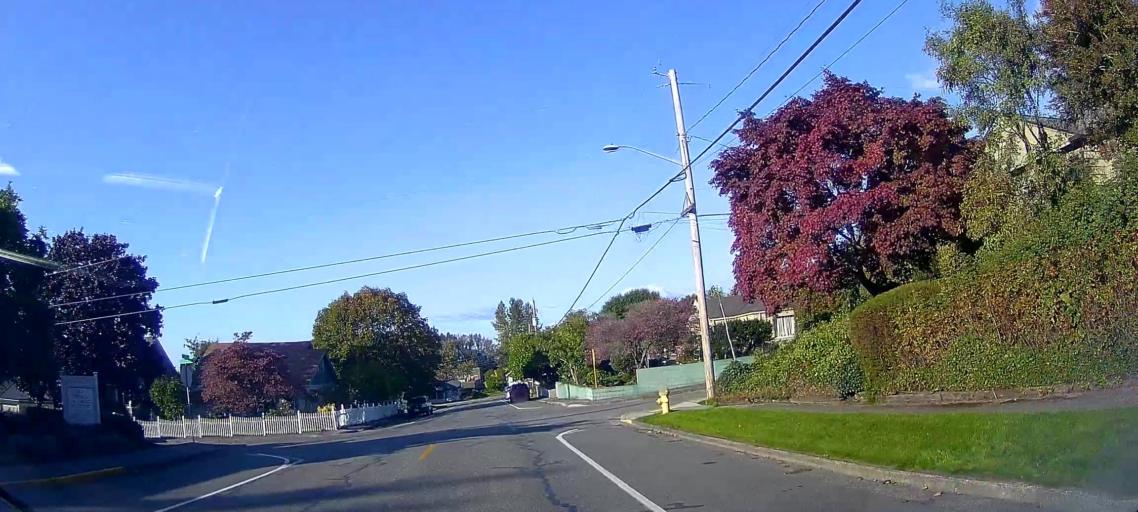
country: US
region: Washington
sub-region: Skagit County
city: Mount Vernon
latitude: 48.4273
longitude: -122.3327
